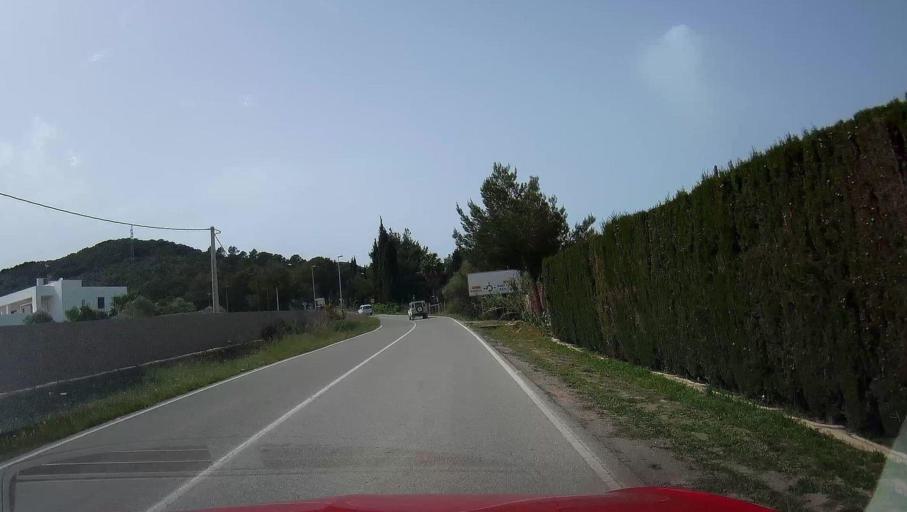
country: ES
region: Balearic Islands
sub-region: Illes Balears
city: Santa Eularia des Riu
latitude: 38.9902
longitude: 1.4868
